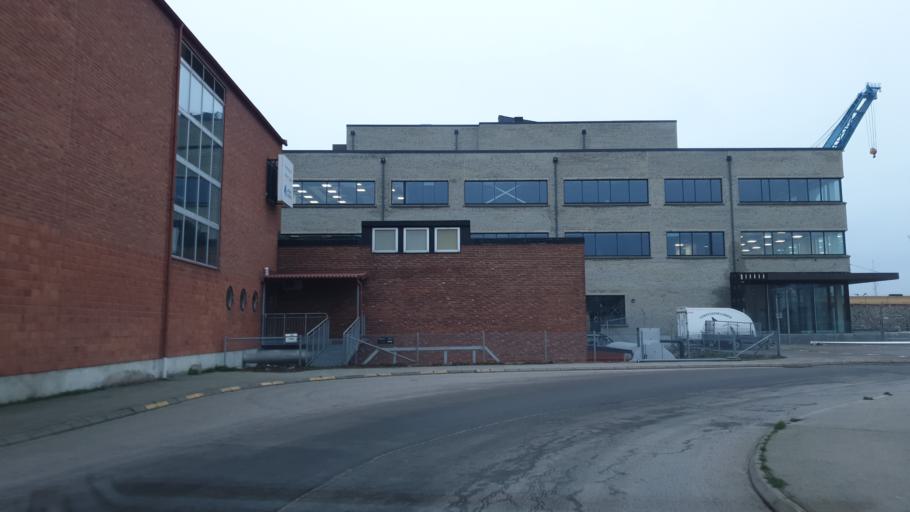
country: SE
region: Blekinge
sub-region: Karlskrona Kommun
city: Karlskrona
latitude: 56.1578
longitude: 15.5795
